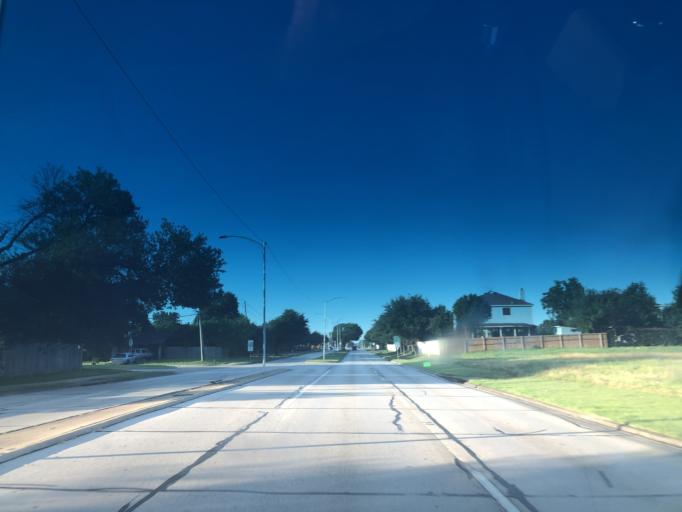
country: US
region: Texas
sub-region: Dallas County
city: Grand Prairie
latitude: 32.7024
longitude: -97.0156
